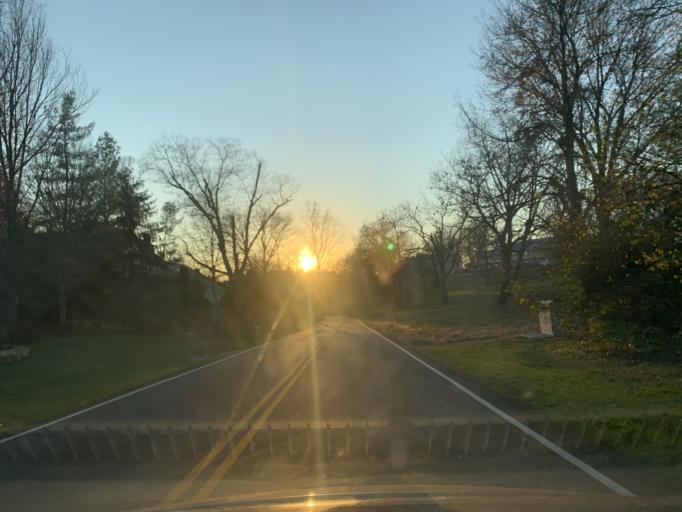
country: US
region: Kentucky
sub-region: Jefferson County
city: Saint Matthews
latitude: 38.2363
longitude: -85.6817
